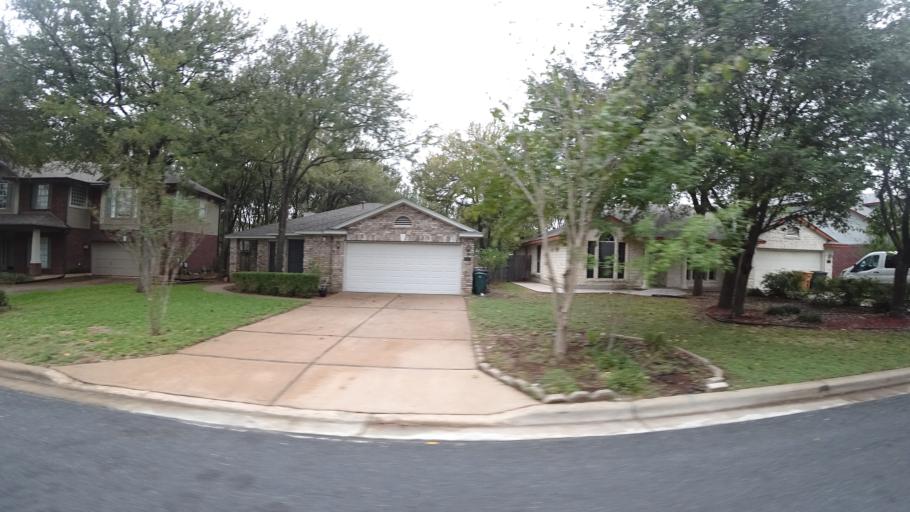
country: US
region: Texas
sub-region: Travis County
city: Shady Hollow
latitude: 30.1876
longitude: -97.8429
